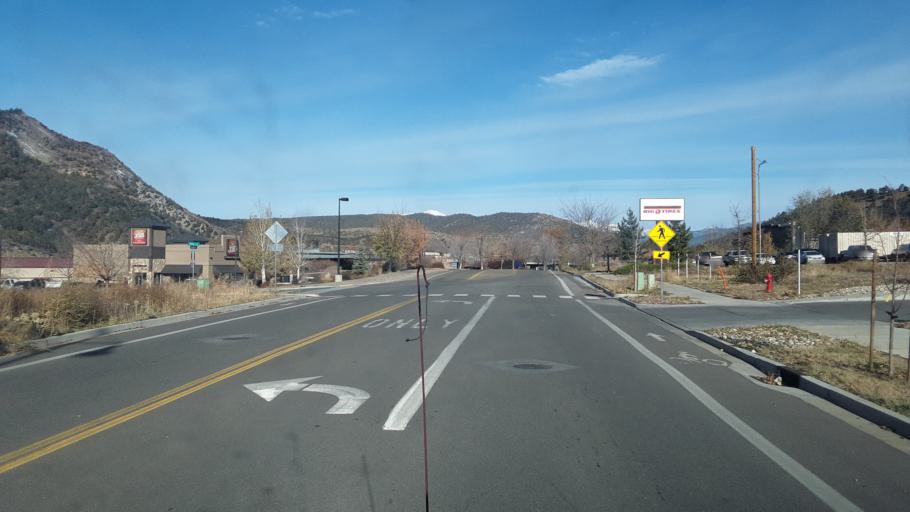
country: US
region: Colorado
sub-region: La Plata County
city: Durango
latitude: 37.2274
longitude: -107.8625
